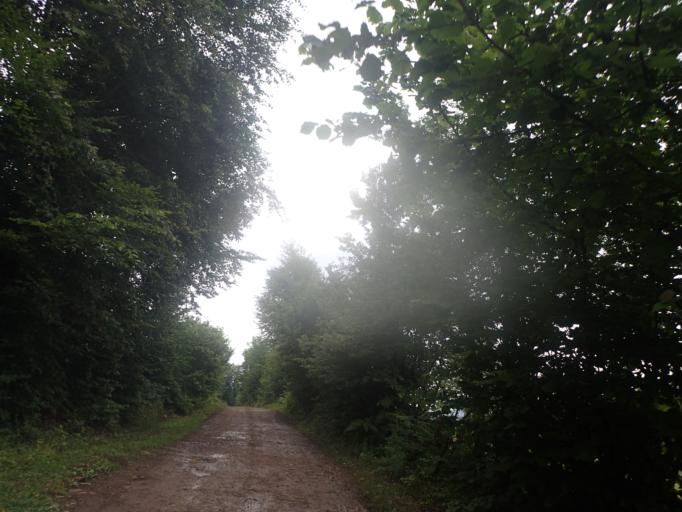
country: TR
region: Ordu
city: Akkus
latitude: 40.8036
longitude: 37.0743
